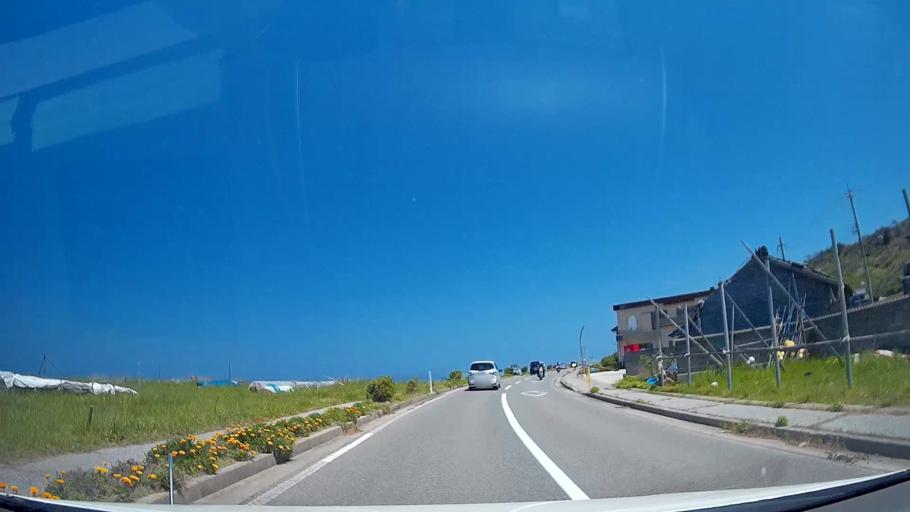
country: JP
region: Ishikawa
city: Nanao
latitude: 37.4836
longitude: 137.1080
